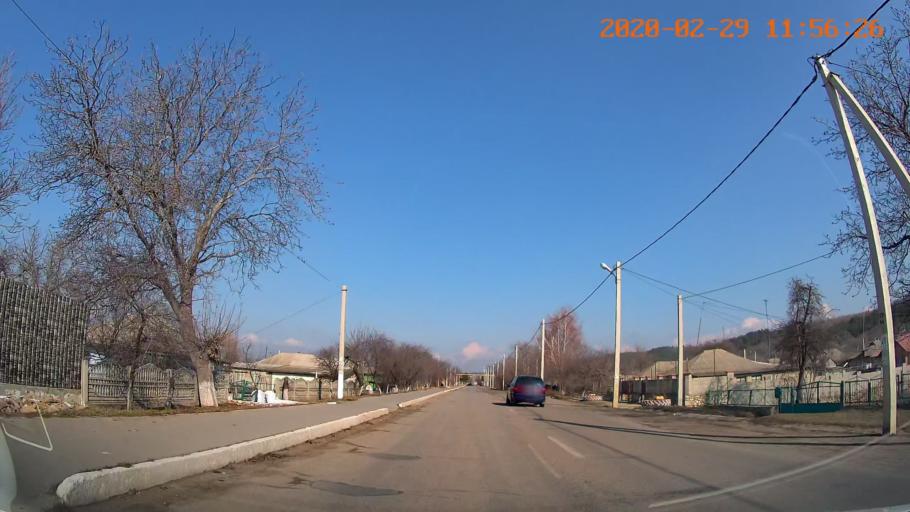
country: MD
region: Telenesti
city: Ribnita
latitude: 47.7966
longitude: 29.0019
